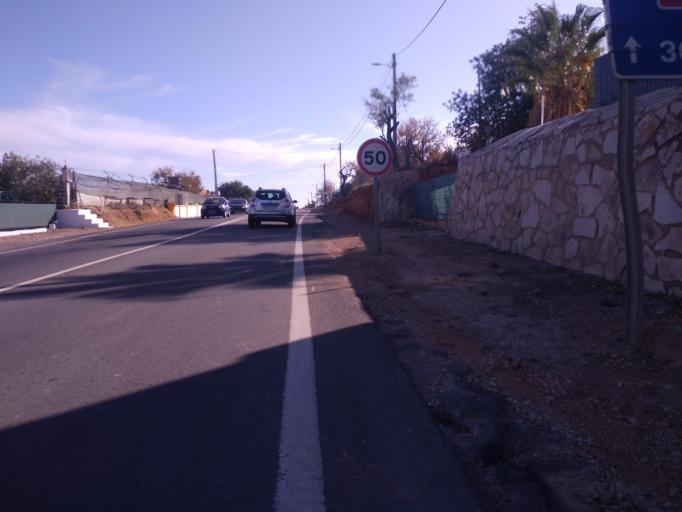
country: PT
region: Faro
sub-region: Sao Bras de Alportel
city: Sao Bras de Alportel
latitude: 37.0960
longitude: -7.9067
